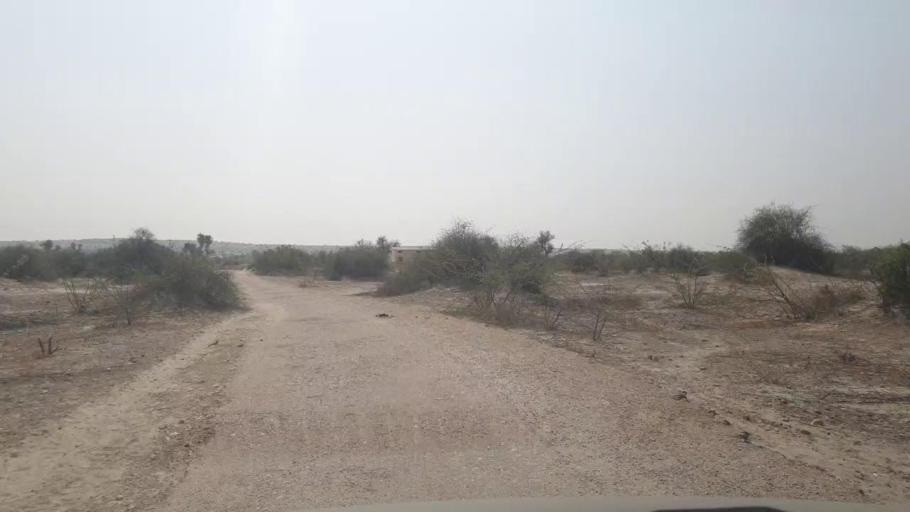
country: PK
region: Sindh
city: Chor
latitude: 25.4542
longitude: 69.7899
